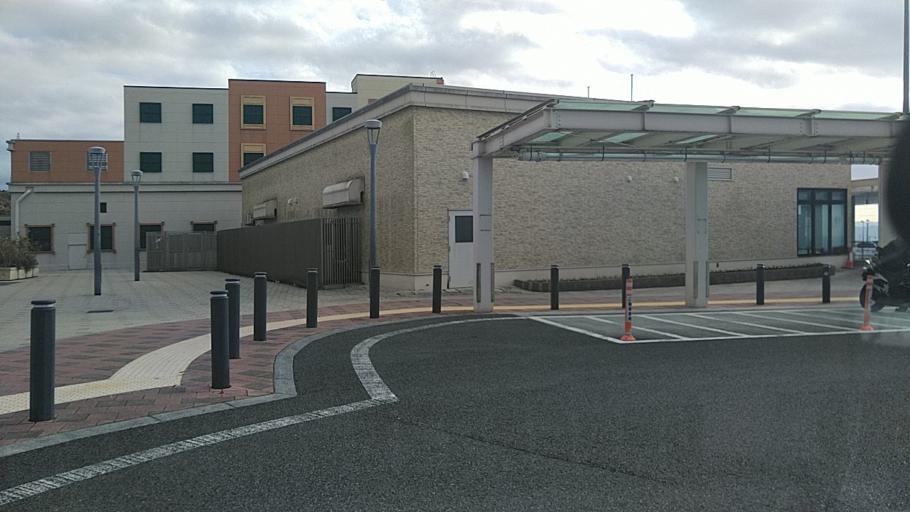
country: JP
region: Shizuoka
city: Numazu
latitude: 35.1548
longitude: 138.8054
